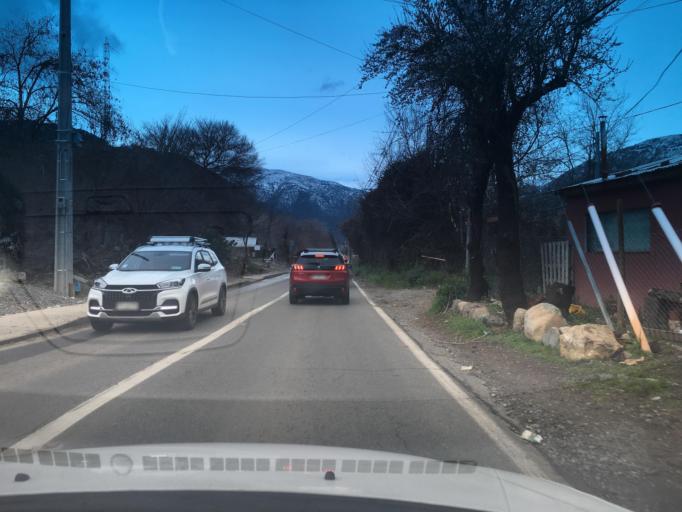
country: CL
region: Santiago Metropolitan
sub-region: Provincia de Cordillera
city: Puente Alto
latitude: -33.5820
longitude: -70.4012
